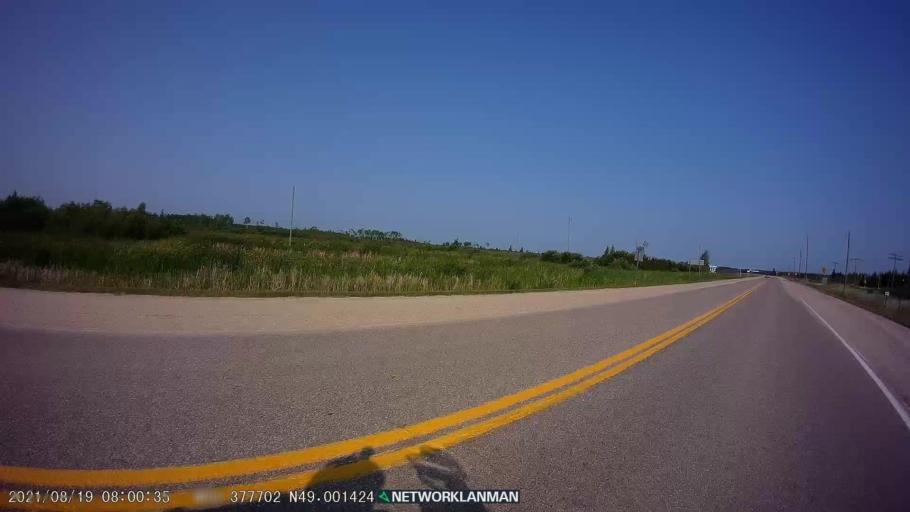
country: US
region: Minnesota
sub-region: Roseau County
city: Warroad
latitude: 49.0020
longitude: -95.3785
